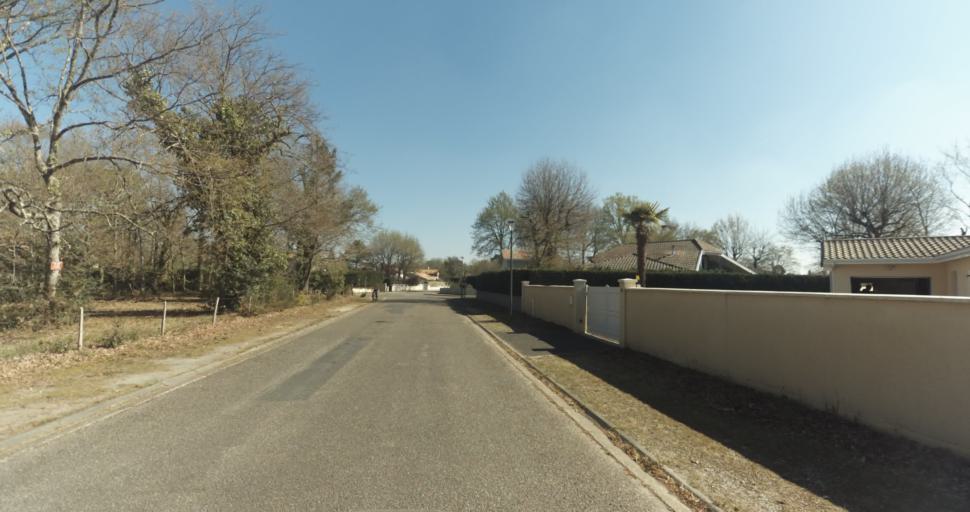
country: FR
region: Aquitaine
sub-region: Departement de la Gironde
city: Martignas-sur-Jalle
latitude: 44.8030
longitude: -0.7916
